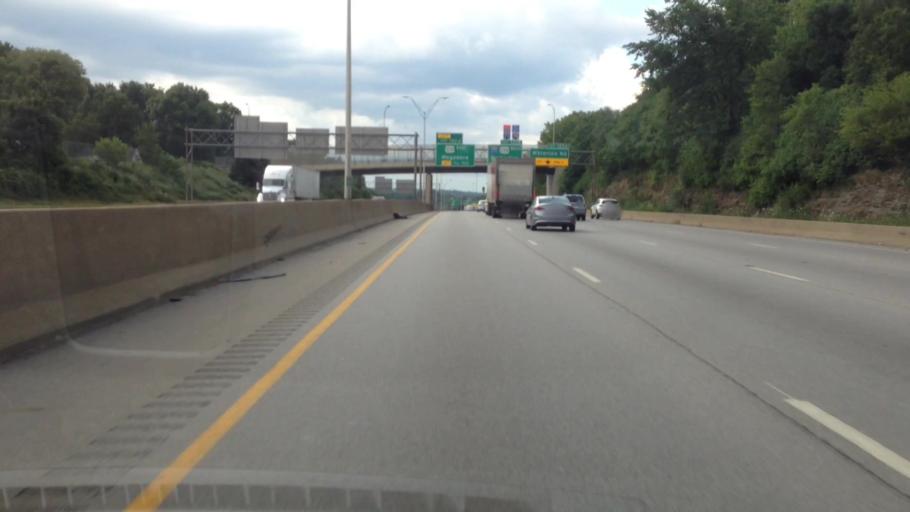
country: US
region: Ohio
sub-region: Summit County
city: Portage Lakes
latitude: 41.0372
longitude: -81.5051
